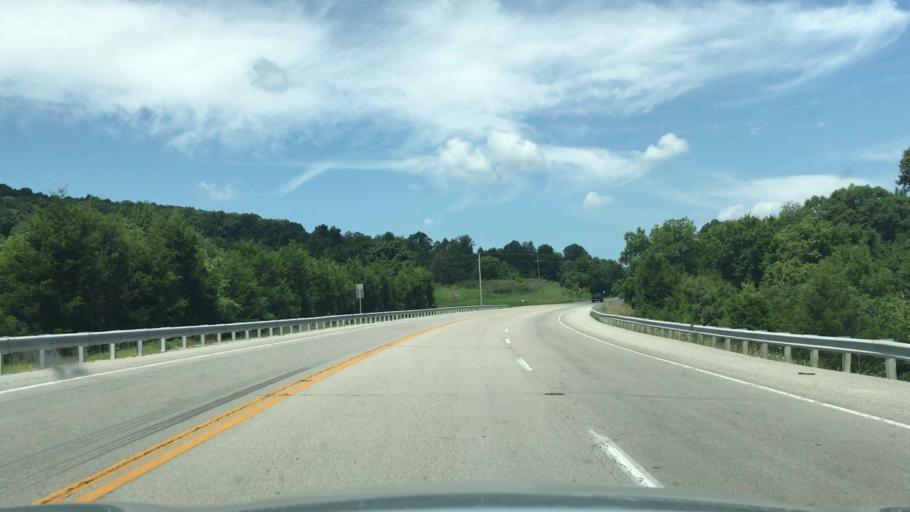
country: US
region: Kentucky
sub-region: Clinton County
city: Albany
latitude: 36.7495
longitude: -85.0858
